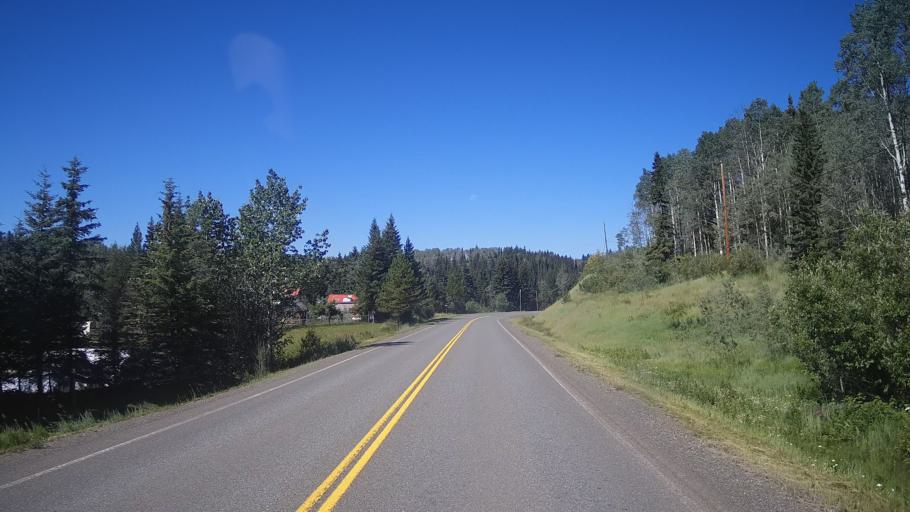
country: CA
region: British Columbia
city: Kamloops
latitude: 51.5029
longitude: -120.6237
